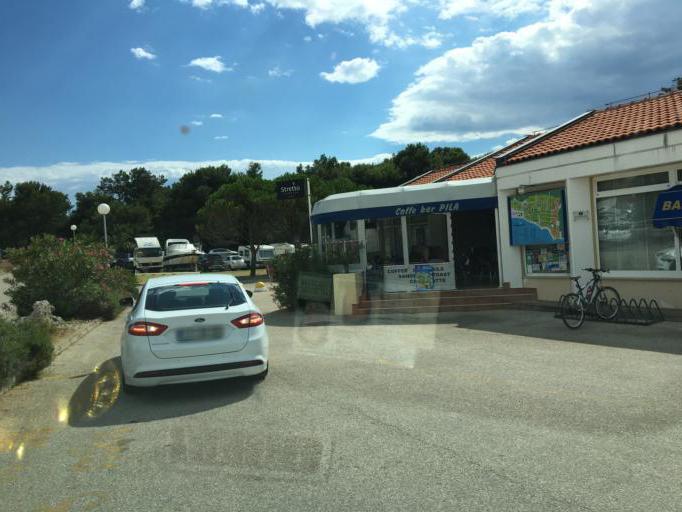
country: HR
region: Primorsko-Goranska
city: Punat
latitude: 45.0160
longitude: 14.6287
